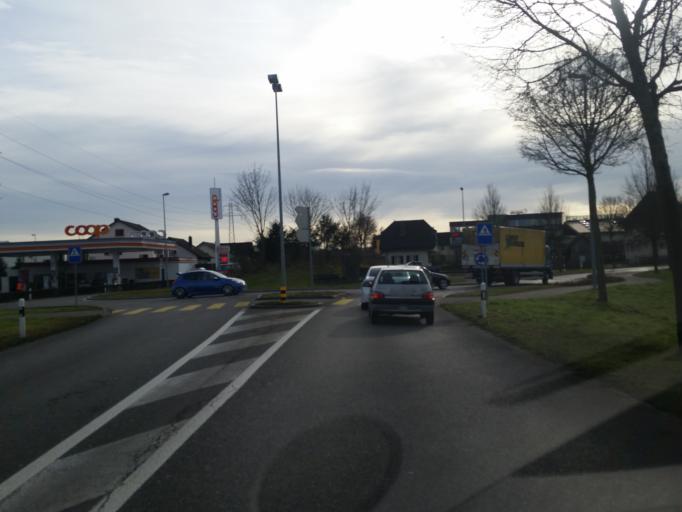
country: CH
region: Aargau
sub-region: Bezirk Bremgarten
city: Dottikon
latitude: 47.3705
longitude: 8.2307
